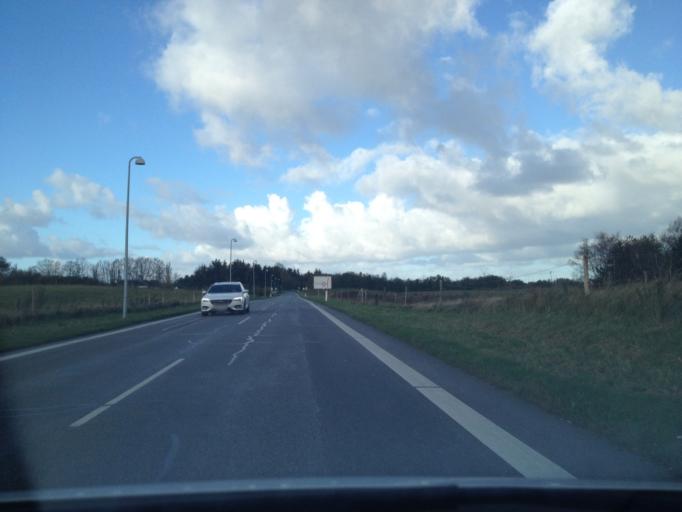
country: DK
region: Capital Region
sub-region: Fureso Kommune
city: Farum
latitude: 55.8329
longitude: 12.3750
